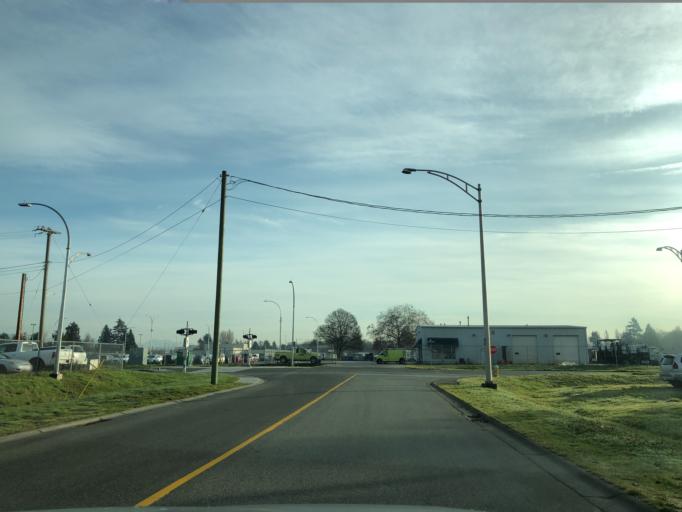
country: CA
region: British Columbia
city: Richmond
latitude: 49.1903
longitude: -123.1550
